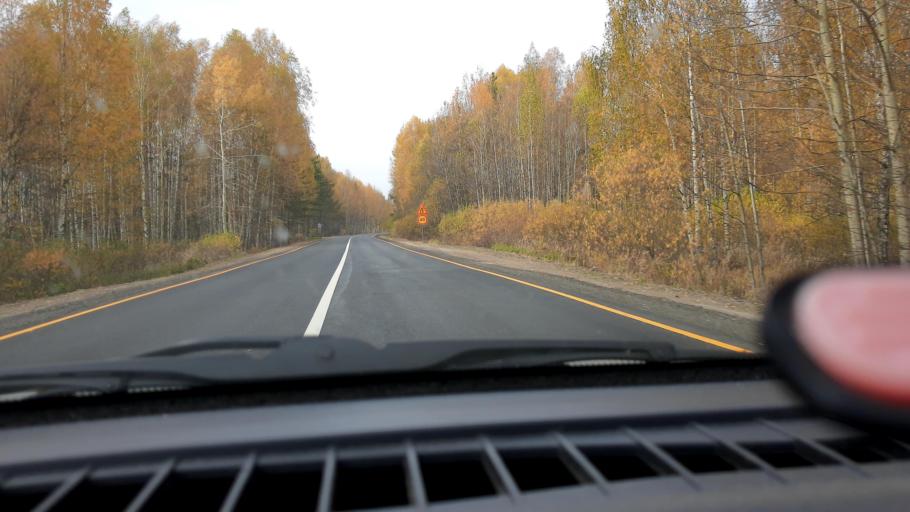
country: RU
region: Nizjnij Novgorod
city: Novaya Balakhna
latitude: 56.5496
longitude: 43.7522
